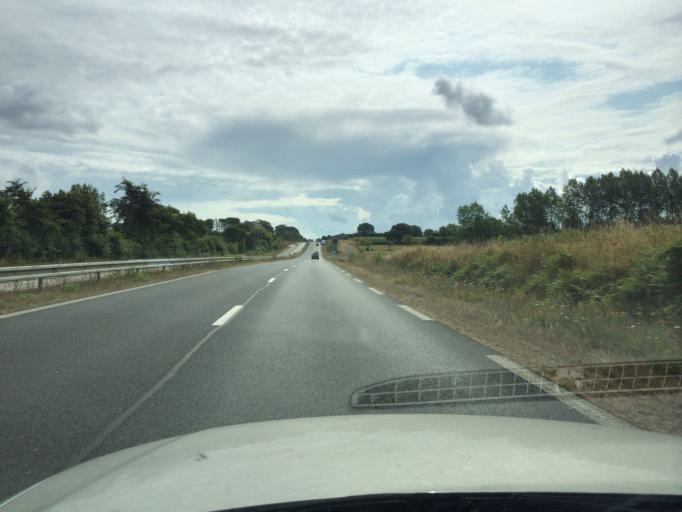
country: FR
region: Lower Normandy
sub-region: Departement de la Manche
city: Valognes
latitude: 49.4971
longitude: -1.4334
